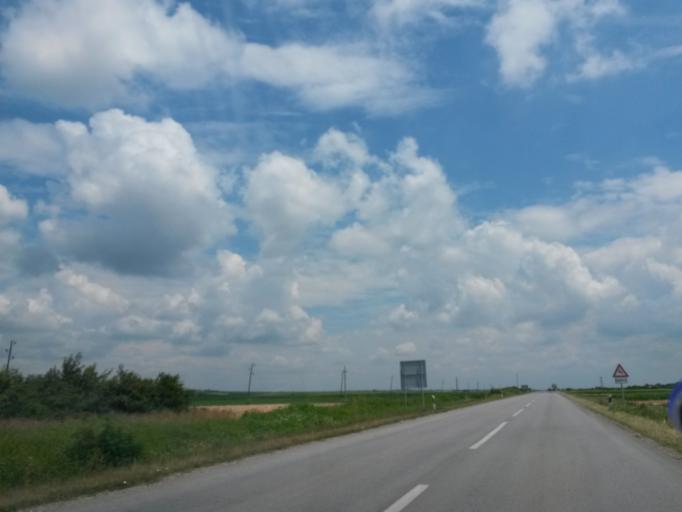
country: HR
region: Osjecko-Baranjska
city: Dalj
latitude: 45.5029
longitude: 18.9834
